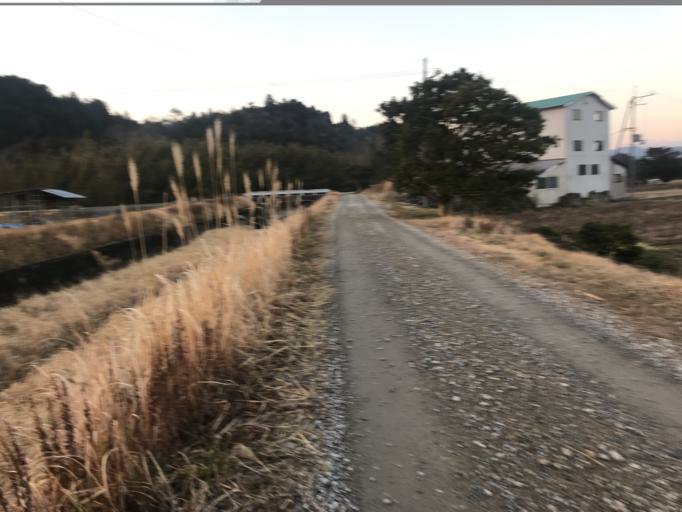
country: JP
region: Kyoto
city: Kameoka
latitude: 35.0018
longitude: 135.5457
